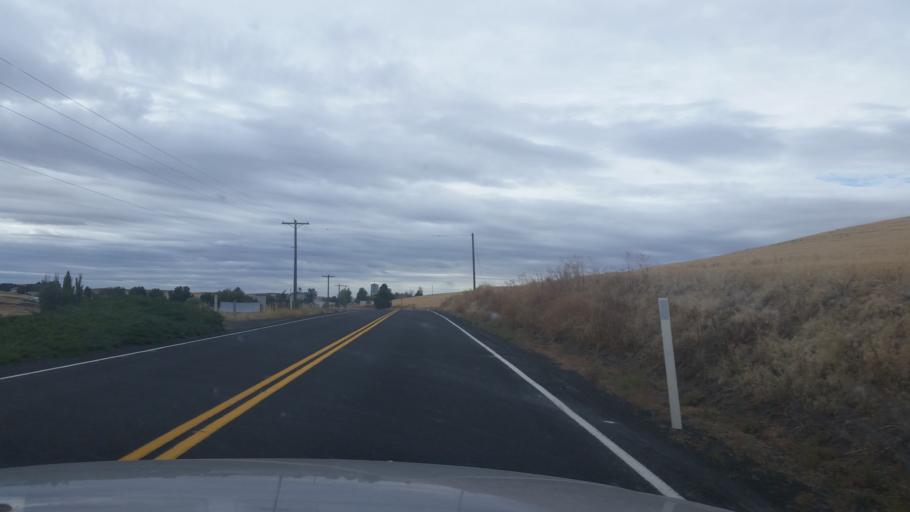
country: US
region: Washington
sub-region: Lincoln County
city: Davenport
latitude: 47.5126
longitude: -117.9429
